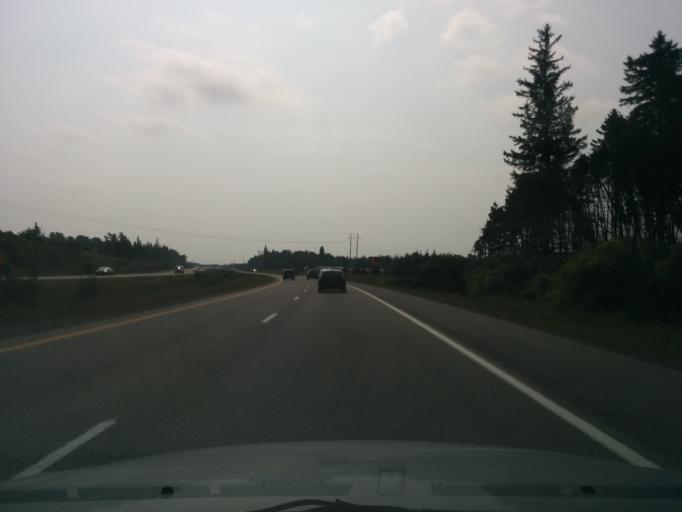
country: CA
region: Ontario
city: Bells Corners
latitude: 45.2820
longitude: -75.8053
